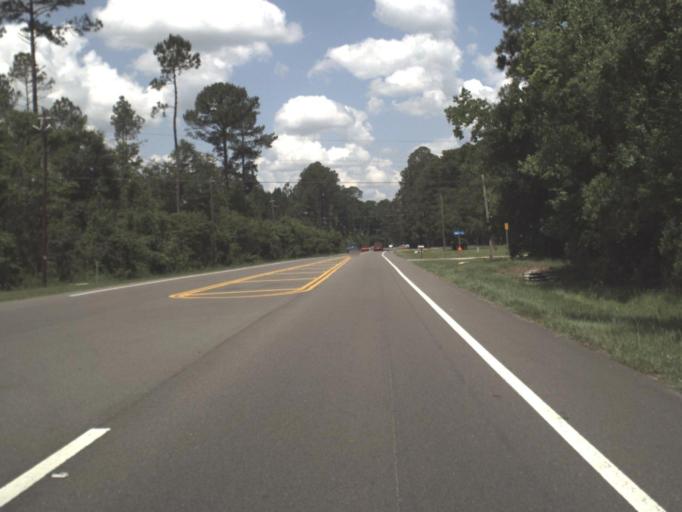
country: US
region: Florida
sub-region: Nassau County
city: Callahan
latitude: 30.5511
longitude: -81.7990
